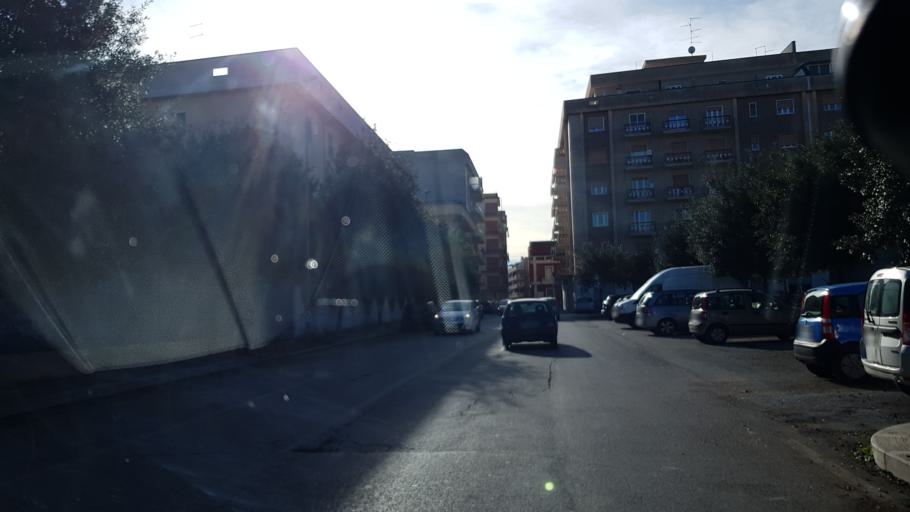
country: IT
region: Apulia
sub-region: Provincia di Bari
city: Gioia del Colle
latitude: 40.8002
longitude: 16.9179
